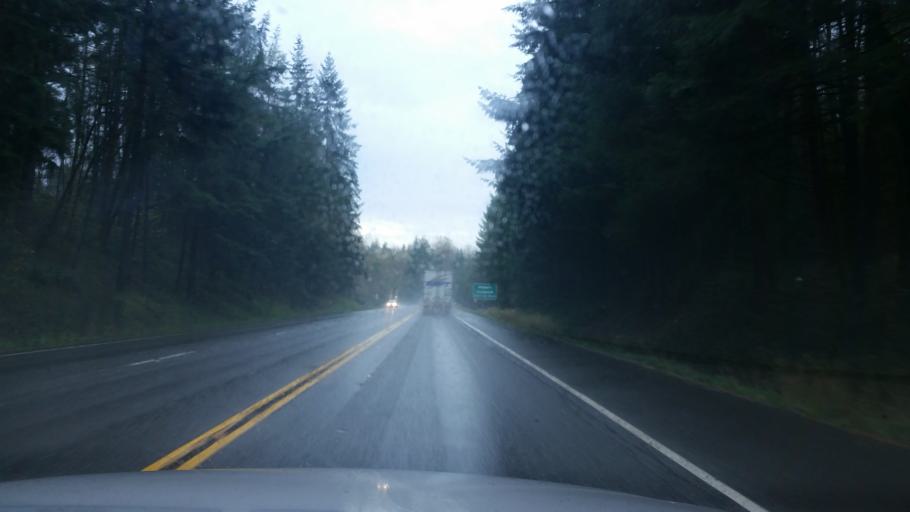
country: US
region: Washington
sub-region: King County
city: Hobart
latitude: 47.4431
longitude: -121.9621
